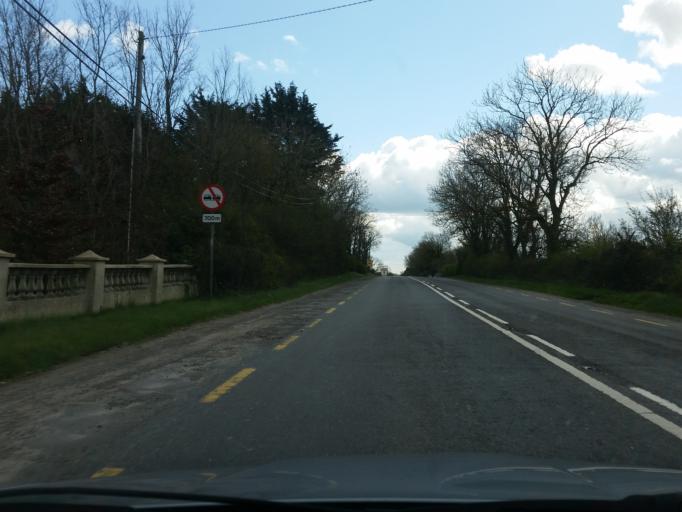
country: IE
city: Kentstown
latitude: 53.6512
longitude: -6.5156
